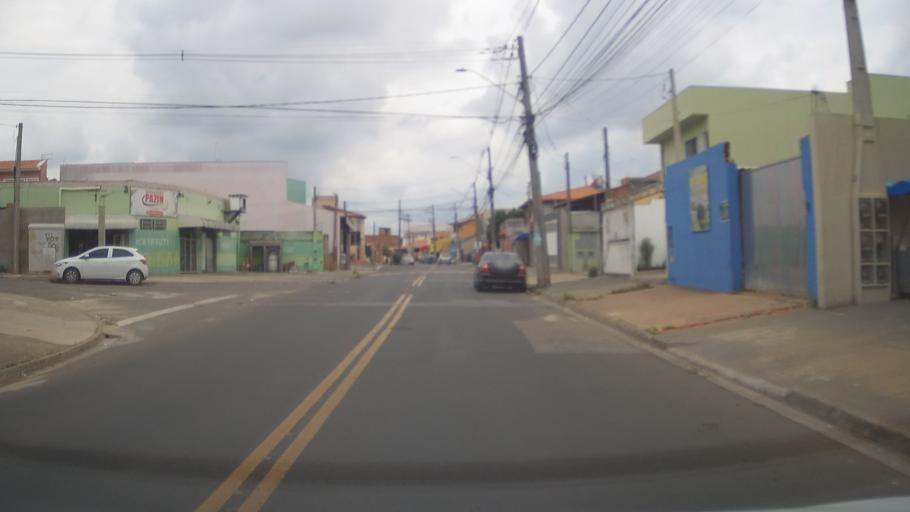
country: BR
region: Sao Paulo
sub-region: Itupeva
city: Itupeva
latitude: -23.1435
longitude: -47.0063
